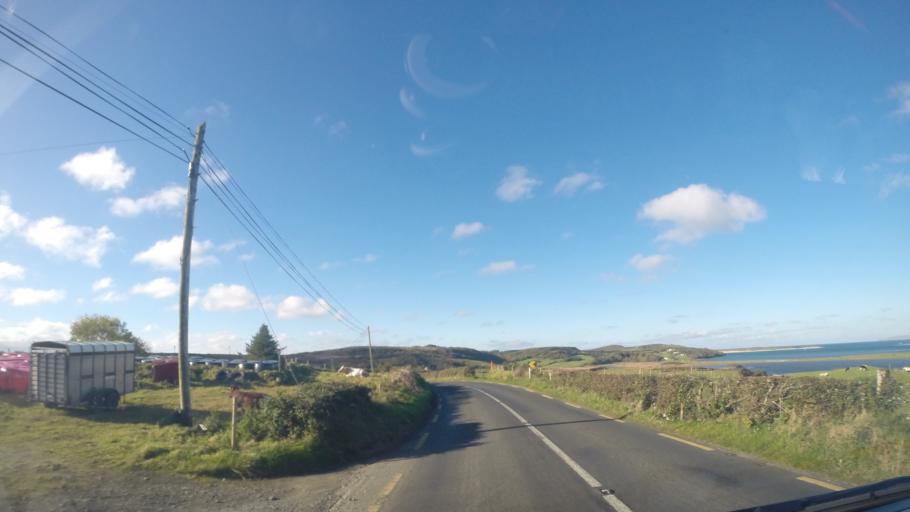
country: IE
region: Ulster
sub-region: County Donegal
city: Dungloe
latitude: 54.8343
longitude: -8.3640
